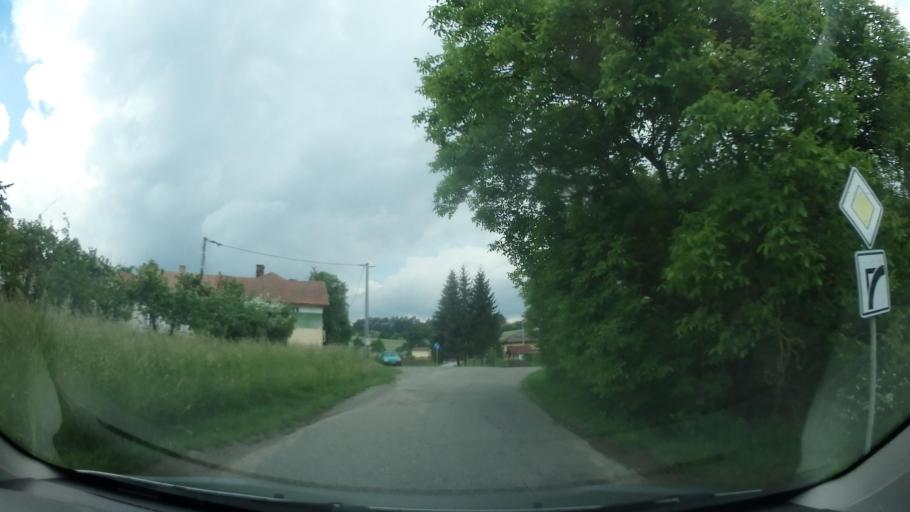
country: CZ
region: South Moravian
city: Boritov
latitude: 49.4487
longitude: 16.5959
